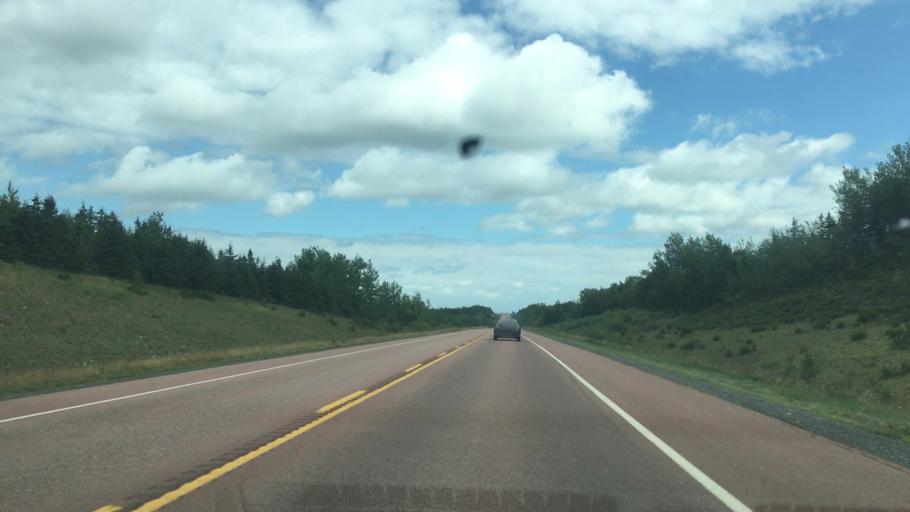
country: CA
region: Nova Scotia
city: Antigonish
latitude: 45.6039
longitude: -61.6889
